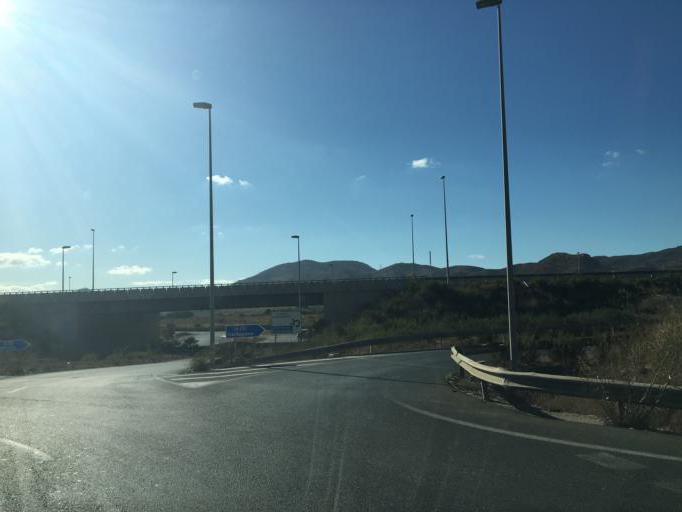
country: ES
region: Murcia
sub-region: Murcia
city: Cartagena
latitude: 37.6172
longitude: -0.9548
